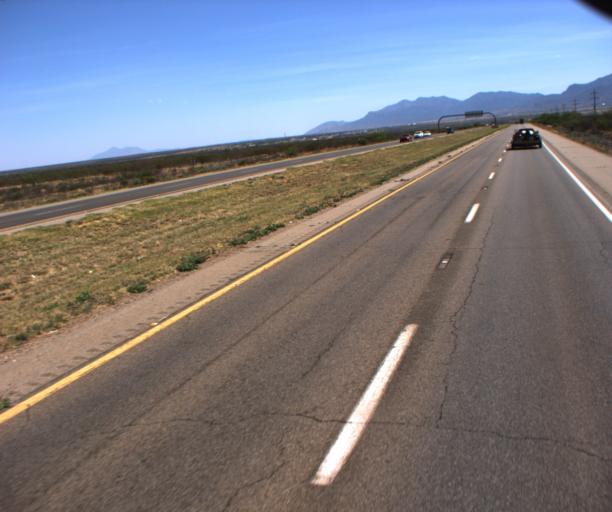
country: US
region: Arizona
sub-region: Cochise County
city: Huachuca City
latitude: 31.6733
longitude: -110.3504
